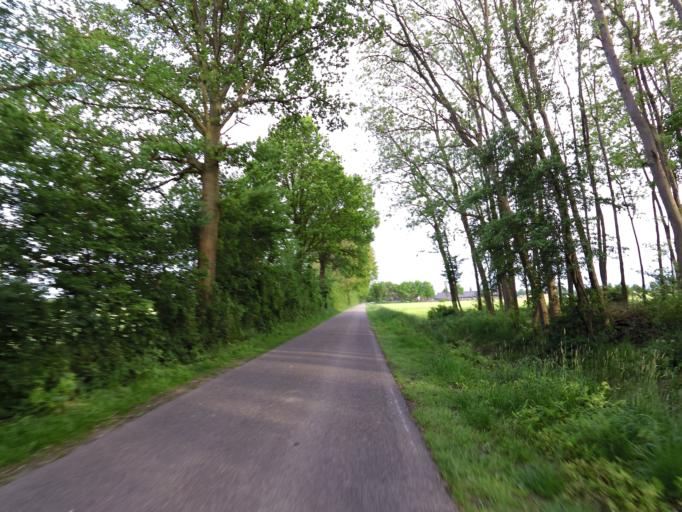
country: NL
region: Gelderland
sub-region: Oude IJsselstreek
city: Gendringen
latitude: 51.8611
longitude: 6.3665
